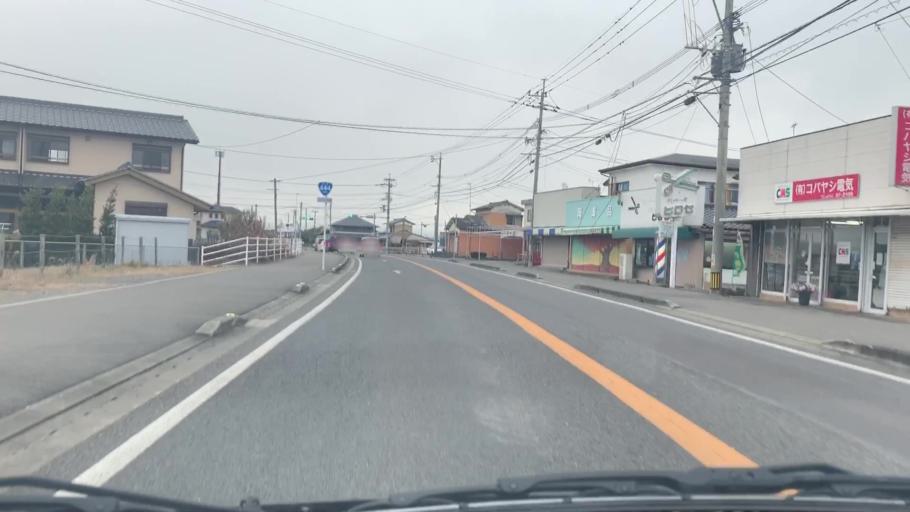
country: JP
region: Saga Prefecture
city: Saga-shi
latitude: 33.1843
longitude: 130.1917
